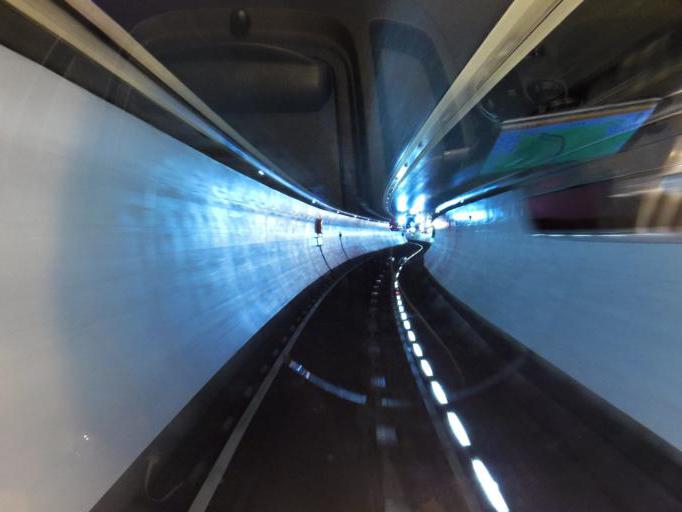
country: CH
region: Grisons
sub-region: Hinterrhein District
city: Thusis
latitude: 46.6601
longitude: 9.4479
